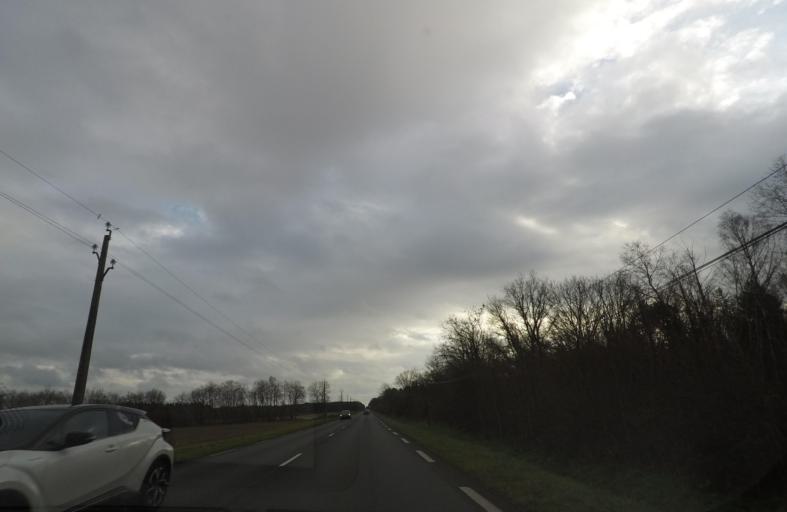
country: FR
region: Centre
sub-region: Departement du Loir-et-Cher
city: Mur-de-Sologne
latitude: 47.4255
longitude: 1.5775
